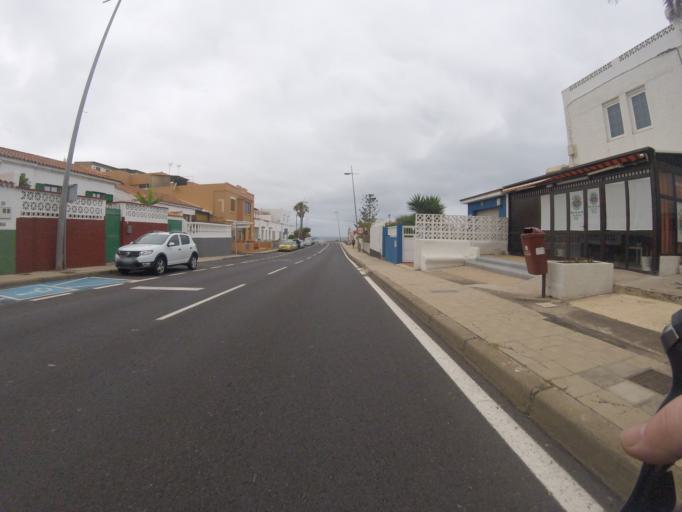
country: ES
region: Canary Islands
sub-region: Provincia de Santa Cruz de Tenerife
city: Tegueste
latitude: 28.5556
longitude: -16.3417
